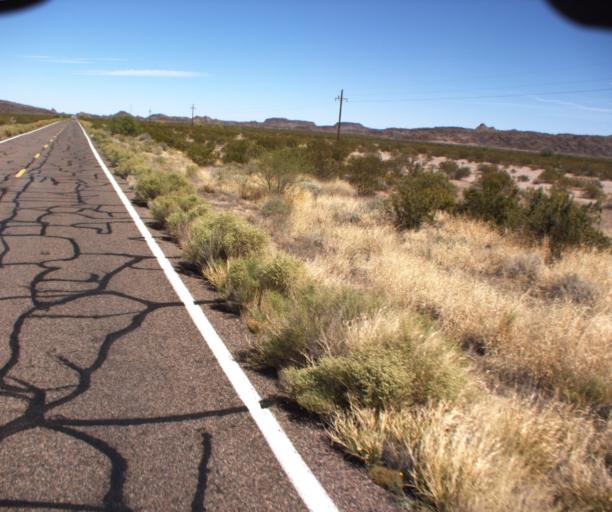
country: US
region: Arizona
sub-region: Pima County
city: Ajo
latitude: 32.5170
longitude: -112.8806
